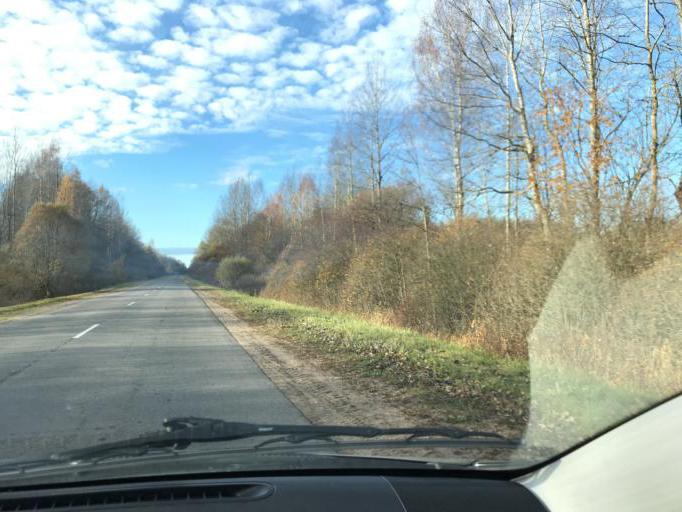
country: BY
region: Vitebsk
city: Haradok
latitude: 55.4247
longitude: 29.8075
